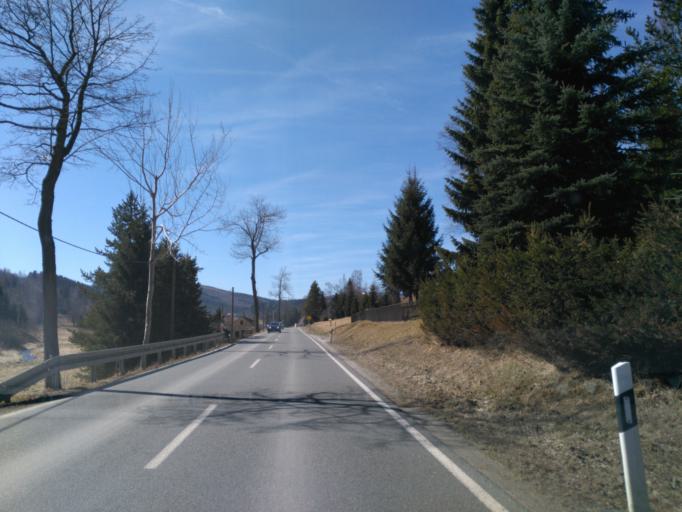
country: CZ
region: Ustecky
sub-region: Okres Chomutov
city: Kovarska
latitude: 50.4512
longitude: 13.0217
